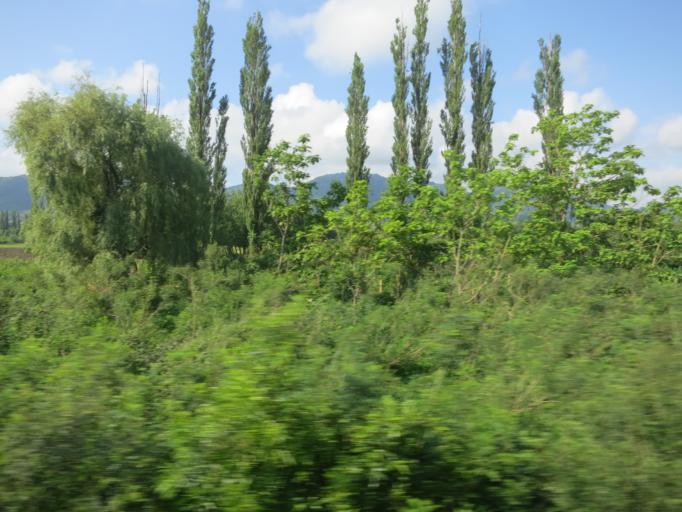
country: GE
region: Guria
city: Lanchkhuti
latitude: 42.0877
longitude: 42.0596
